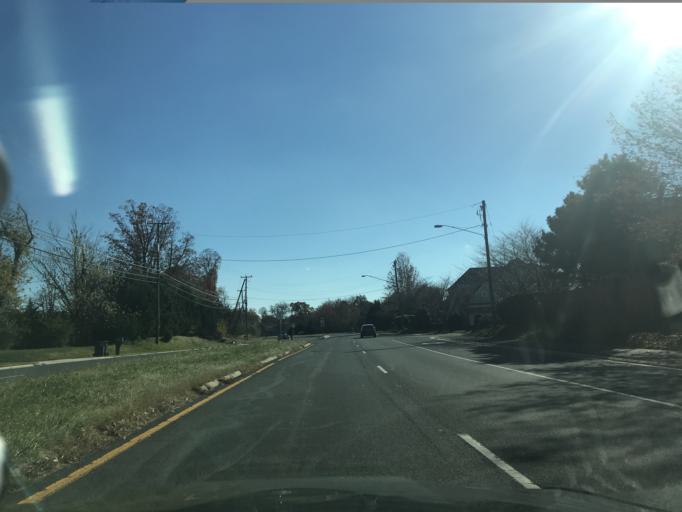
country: US
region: Virginia
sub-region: Fairfax County
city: Greenbriar
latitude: 38.8870
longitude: -77.3763
